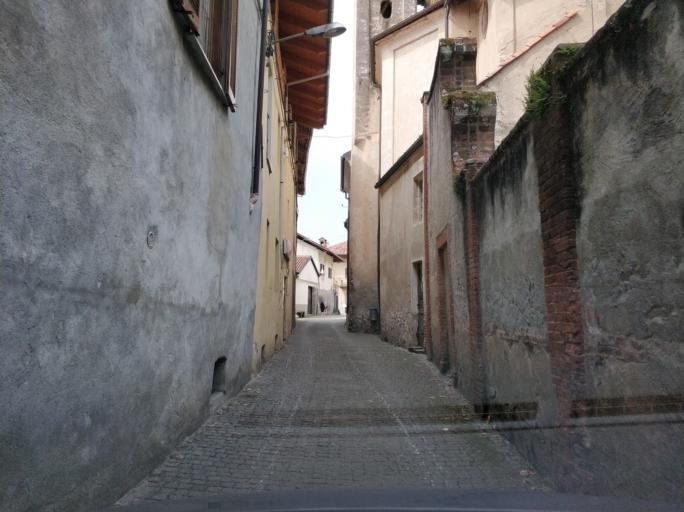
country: IT
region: Piedmont
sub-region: Provincia di Torino
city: Levone
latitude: 45.3185
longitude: 7.6068
